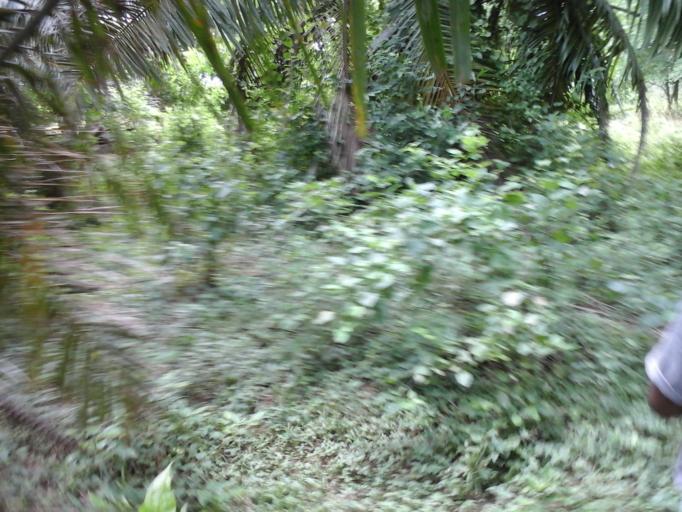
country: CO
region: Bolivar
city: Mahates
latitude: 10.1636
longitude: -75.2760
